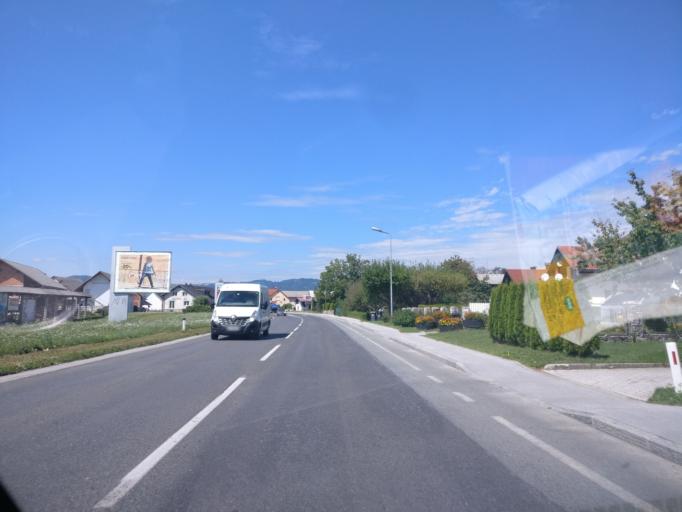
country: SI
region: Skofja Loka
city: Sv. Duh
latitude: 46.1652
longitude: 14.3556
